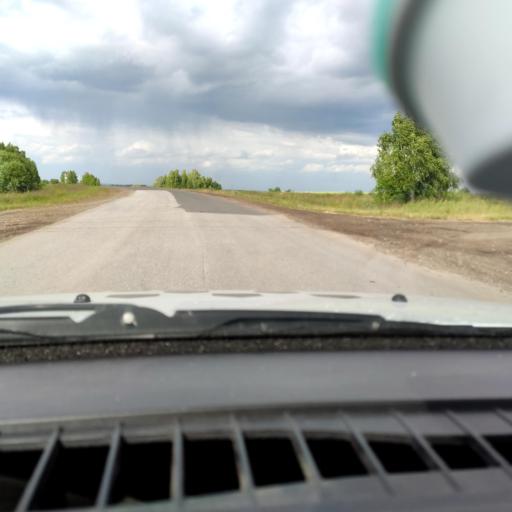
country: RU
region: Perm
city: Orda
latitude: 57.1658
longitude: 56.8184
